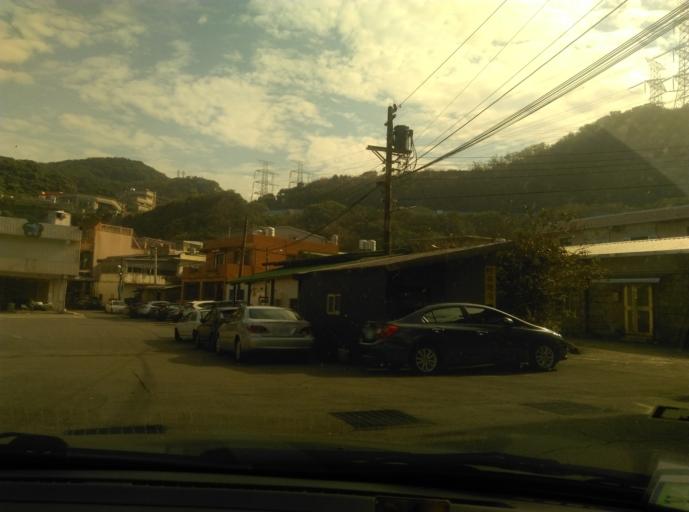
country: TW
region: Taiwan
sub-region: Keelung
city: Keelung
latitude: 25.1586
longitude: 121.7330
